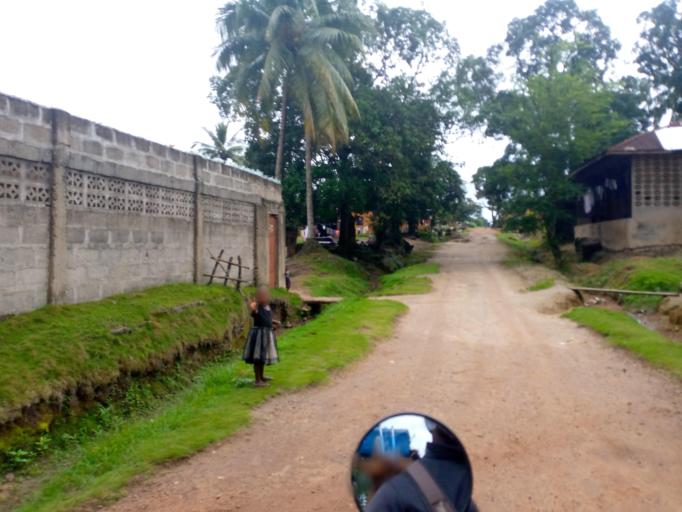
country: SL
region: Eastern Province
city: Kenema
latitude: 7.8640
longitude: -11.1935
